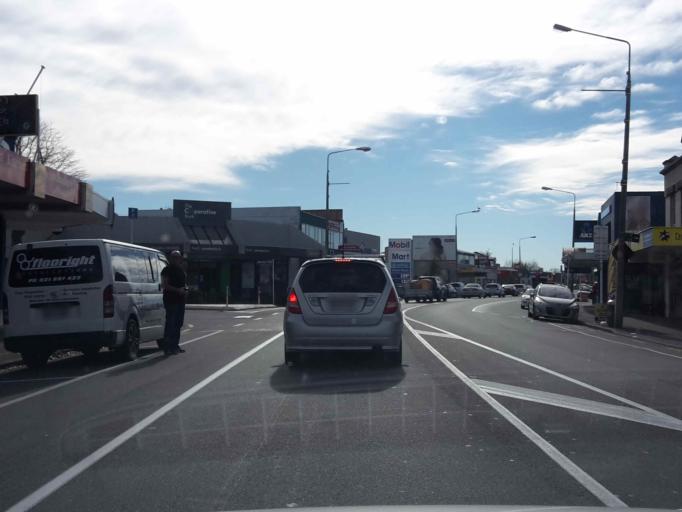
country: NZ
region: Canterbury
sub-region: Christchurch City
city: Christchurch
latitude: -43.4965
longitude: 172.6079
